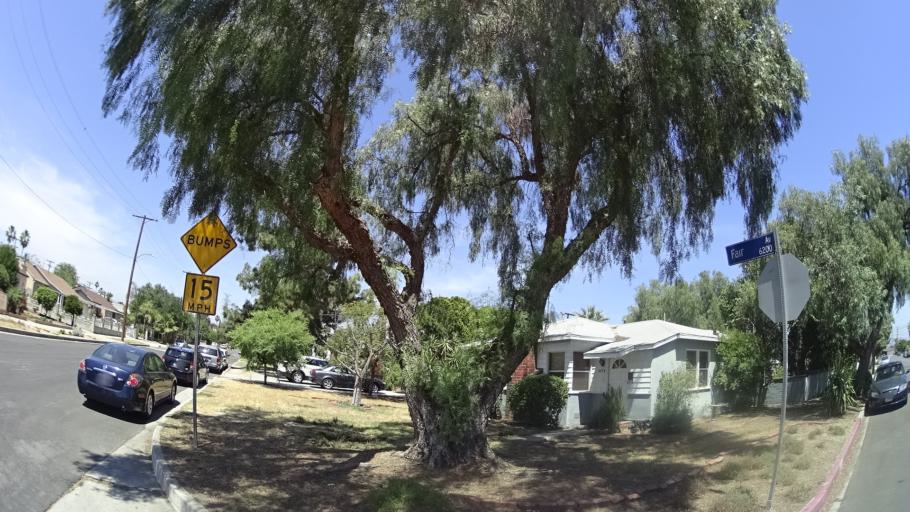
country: US
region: California
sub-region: Los Angeles County
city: North Hollywood
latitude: 34.1839
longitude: -118.3746
